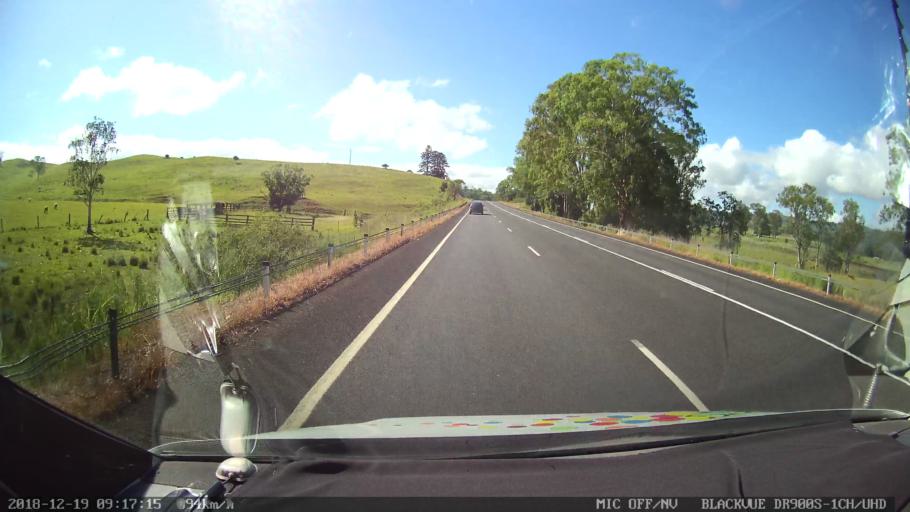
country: AU
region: New South Wales
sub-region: Kyogle
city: Kyogle
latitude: -28.5309
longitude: 152.9731
